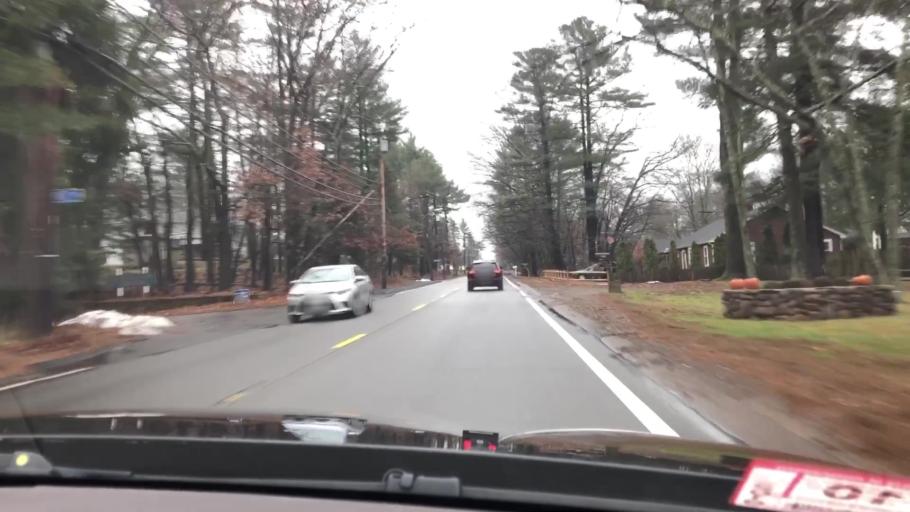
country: US
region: Massachusetts
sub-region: Norfolk County
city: Walpole
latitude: 42.1245
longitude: -71.2706
